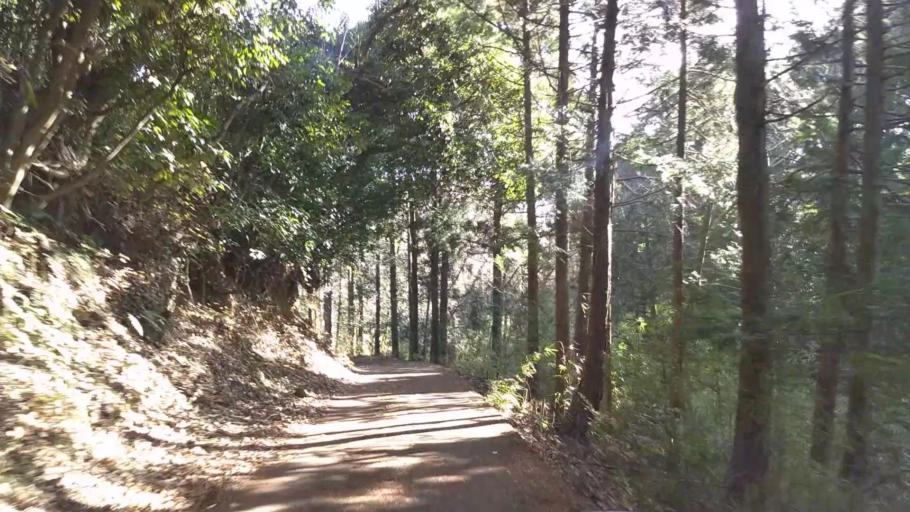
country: JP
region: Kanagawa
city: Isehara
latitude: 35.4424
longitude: 139.2894
